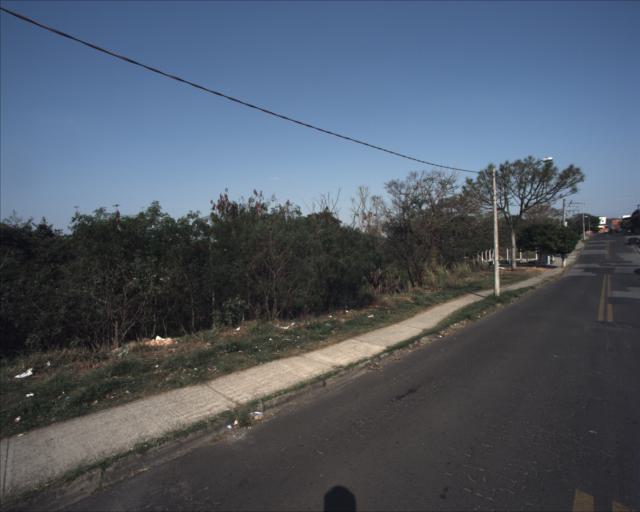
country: BR
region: Sao Paulo
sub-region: Sorocaba
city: Sorocaba
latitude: -23.4267
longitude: -47.4645
